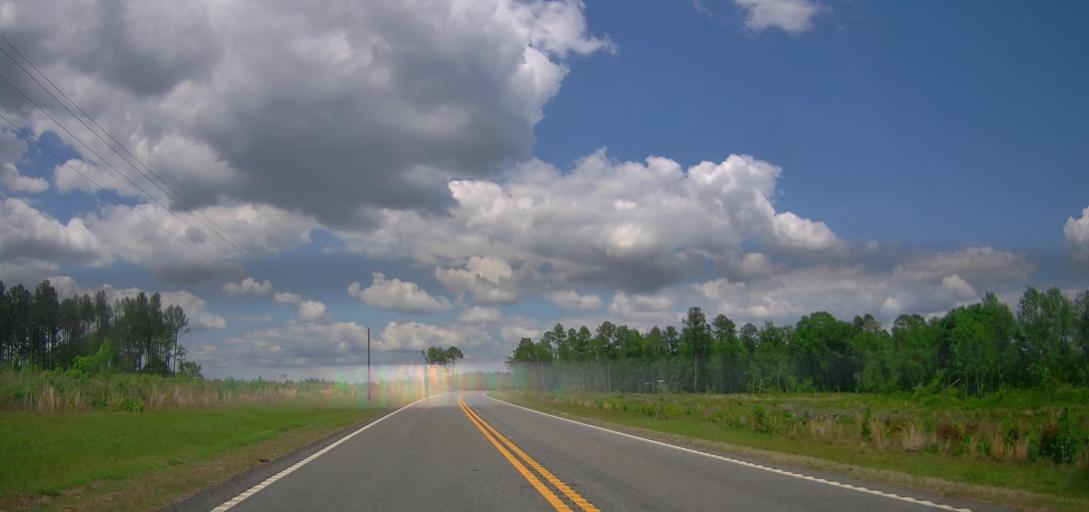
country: US
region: Georgia
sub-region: Treutlen County
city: Soperton
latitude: 32.4111
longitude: -82.6080
